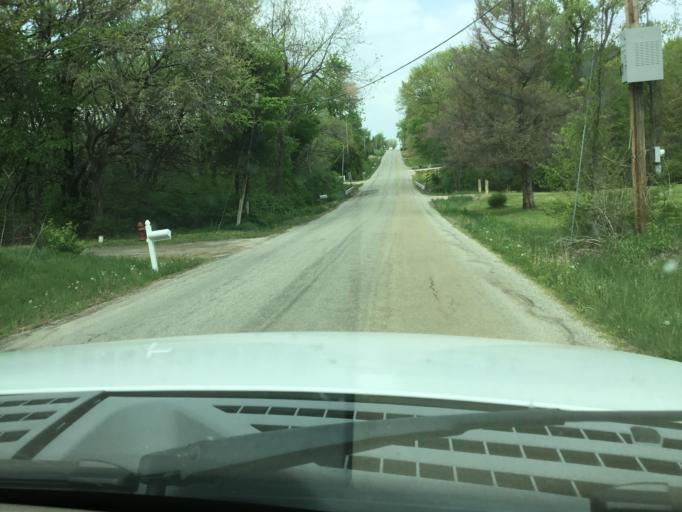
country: US
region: Kansas
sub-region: Shawnee County
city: Topeka
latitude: 38.9824
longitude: -95.5864
